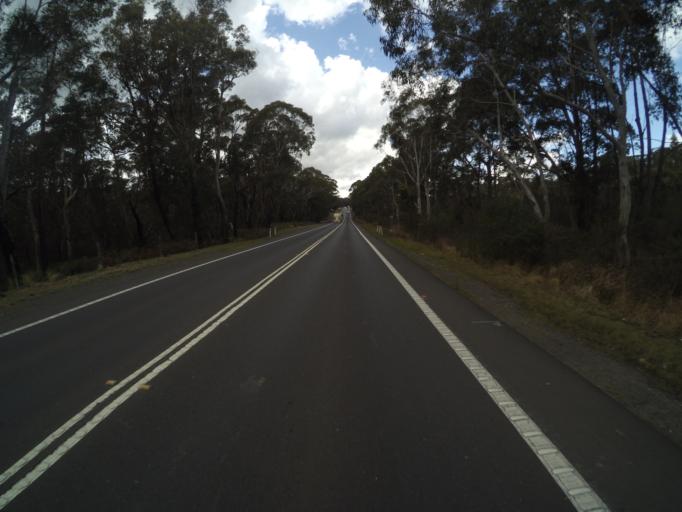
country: AU
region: New South Wales
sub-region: Wollondilly
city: Douglas Park
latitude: -34.3125
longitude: 150.7448
